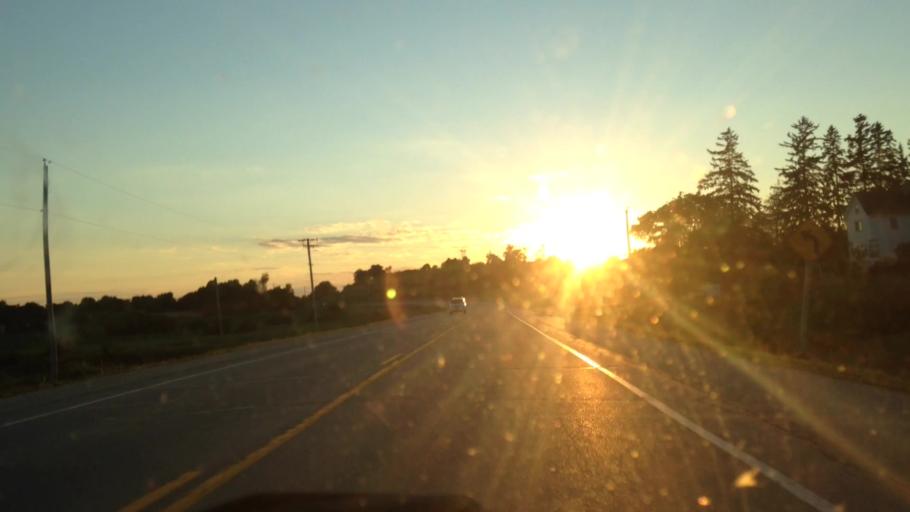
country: US
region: Wisconsin
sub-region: Dodge County
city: Mayville
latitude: 43.4421
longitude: -88.4887
